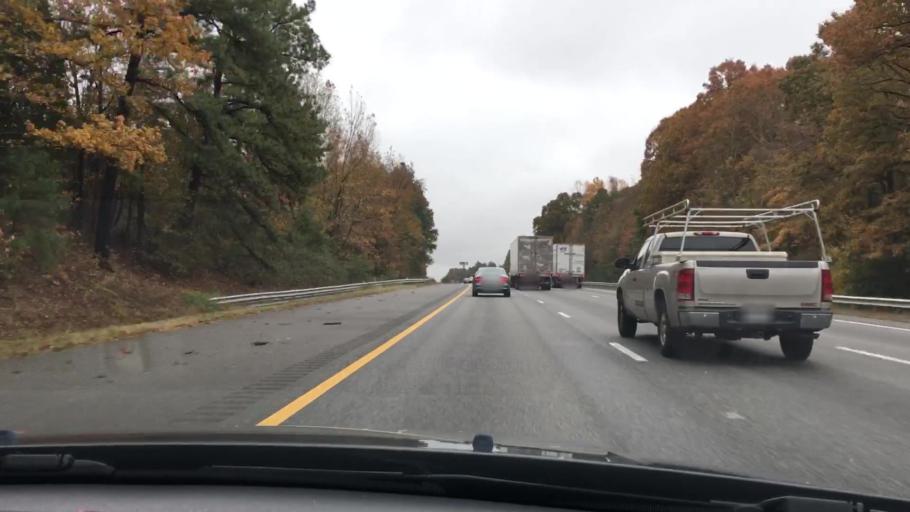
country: US
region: Virginia
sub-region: Caroline County
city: Bowling Green
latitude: 37.9458
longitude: -77.4784
